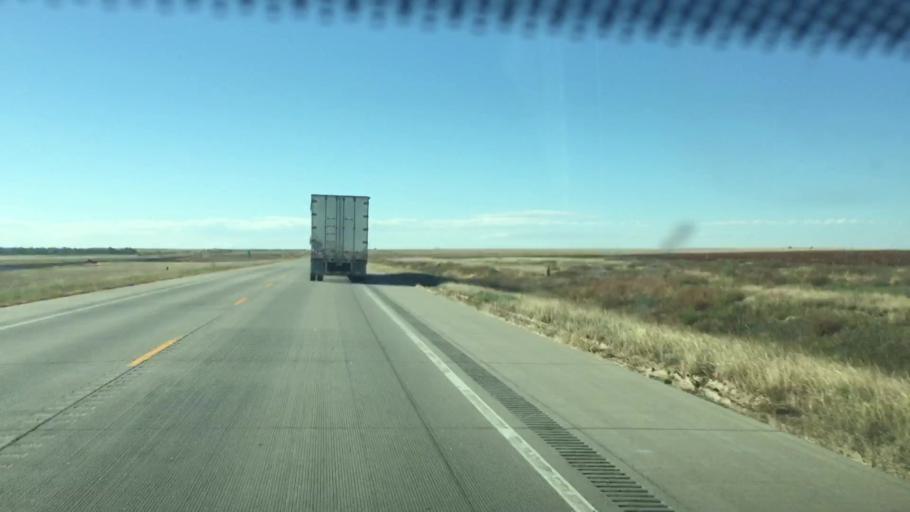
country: US
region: Colorado
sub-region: Kiowa County
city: Eads
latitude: 38.7998
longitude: -102.9553
